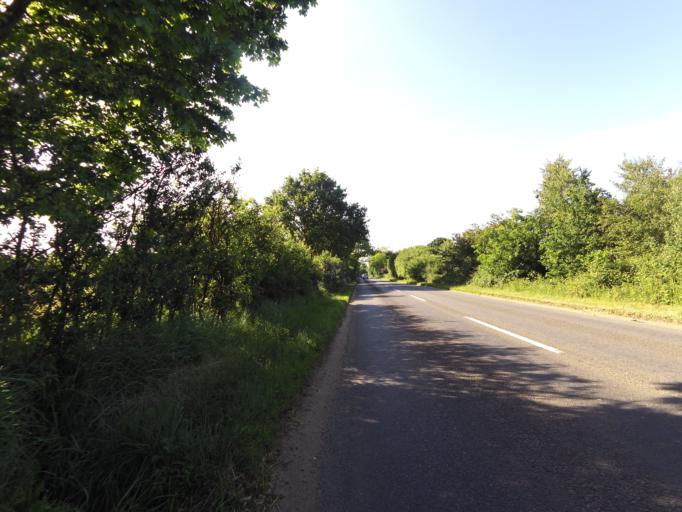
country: GB
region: England
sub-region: Suffolk
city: Woodbridge
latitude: 52.0936
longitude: 1.3514
